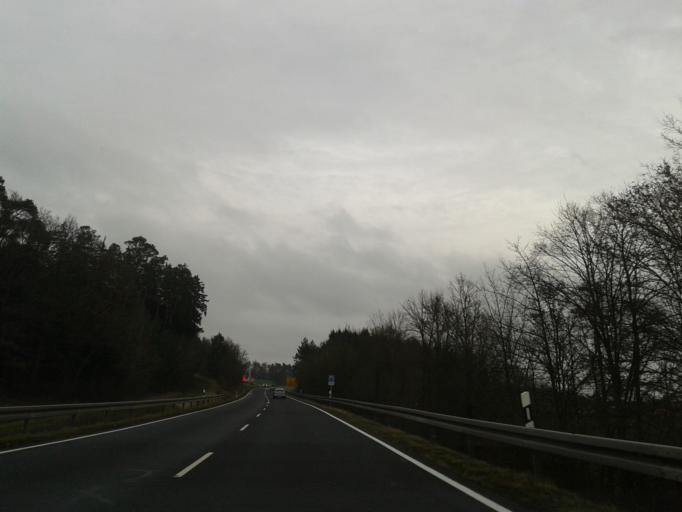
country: DE
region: Bavaria
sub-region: Regierungsbezirk Unterfranken
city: Burgpreppach
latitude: 50.1380
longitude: 10.6345
